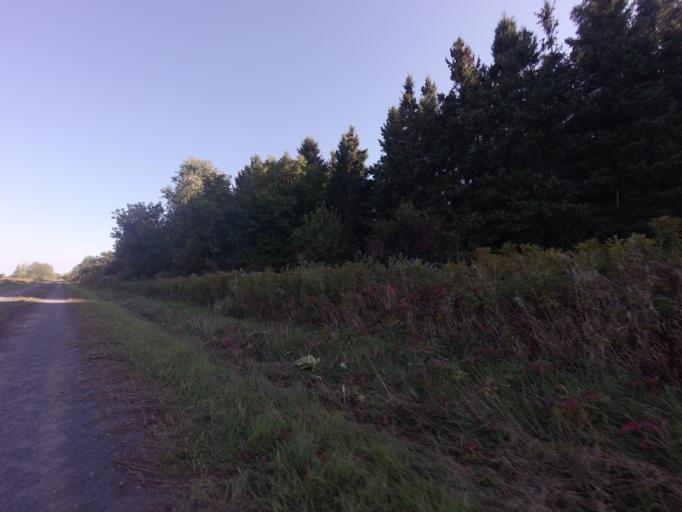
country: CA
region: Ontario
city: Hawkesbury
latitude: 45.5186
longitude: -74.5261
